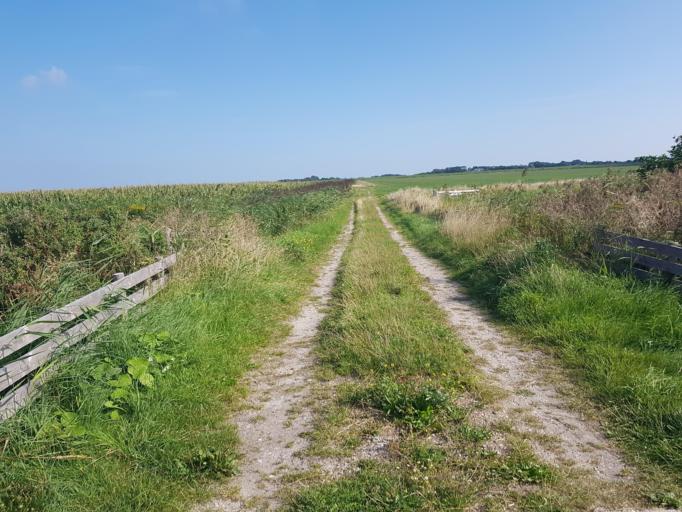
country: NL
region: North Holland
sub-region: Gemeente Texel
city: Den Burg
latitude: 53.1104
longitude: 4.8569
